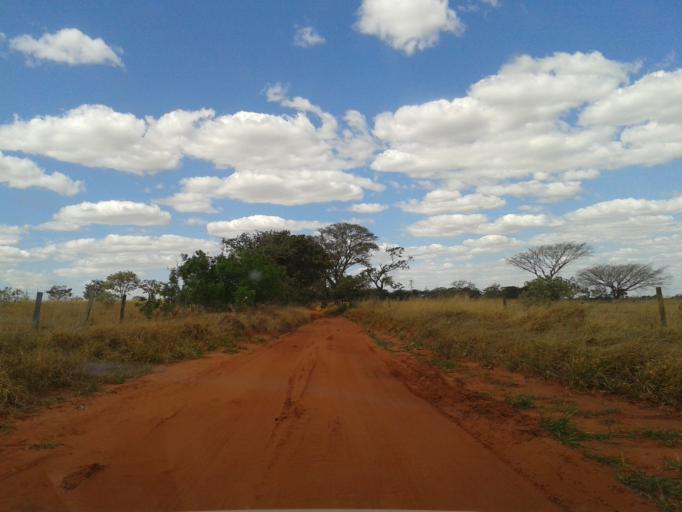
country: BR
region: Minas Gerais
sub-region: Monte Alegre De Minas
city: Monte Alegre de Minas
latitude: -18.7766
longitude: -49.0823
